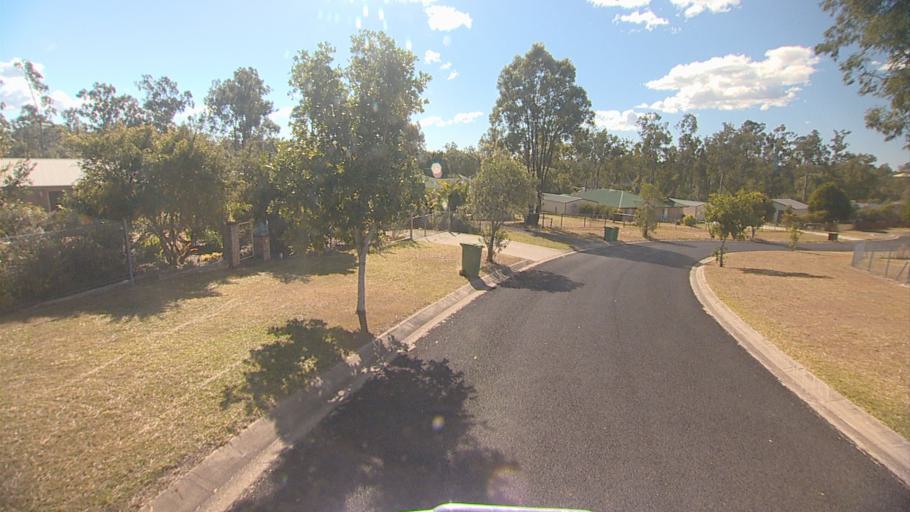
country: AU
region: Queensland
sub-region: Logan
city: North Maclean
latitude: -27.7518
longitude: 152.9376
